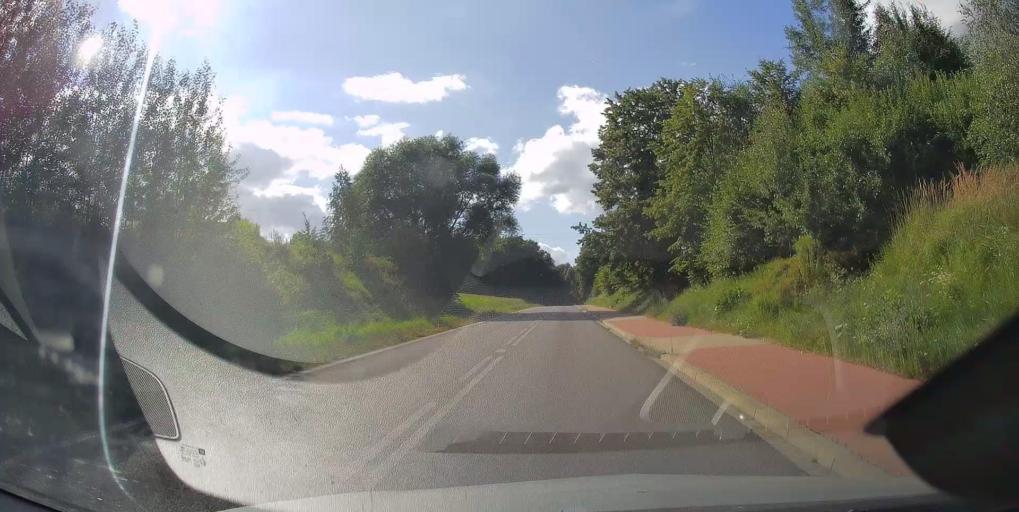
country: PL
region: Swietokrzyskie
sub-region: Powiat kielecki
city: Nowa Slupia
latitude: 50.8678
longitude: 21.0812
